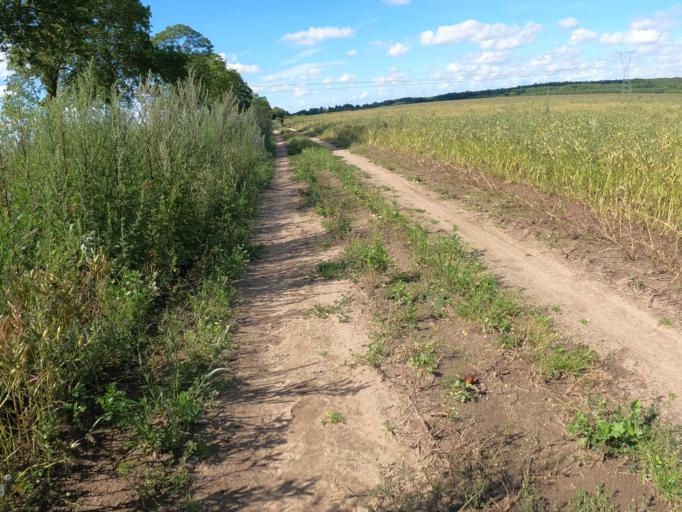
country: PL
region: West Pomeranian Voivodeship
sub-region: Powiat bialogardzki
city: Karlino
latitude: 53.9844
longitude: 15.8618
